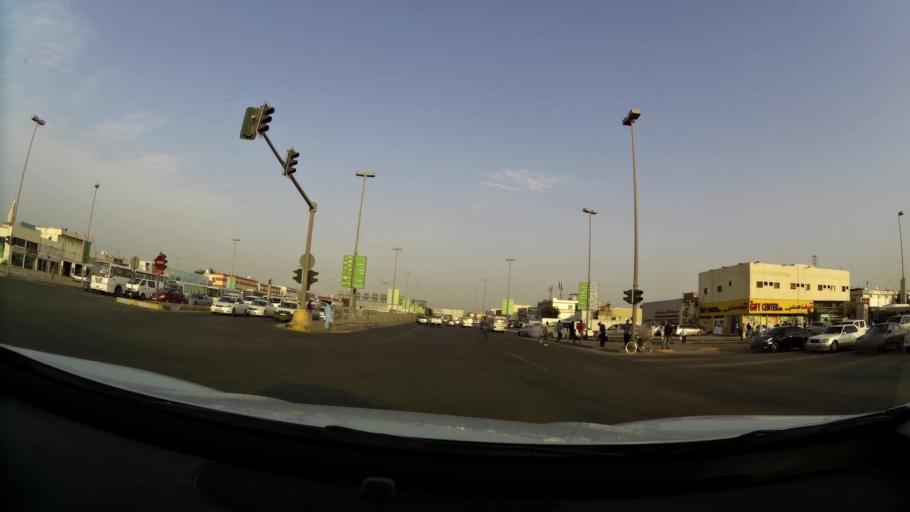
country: AE
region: Abu Dhabi
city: Abu Dhabi
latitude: 24.3731
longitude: 54.5111
